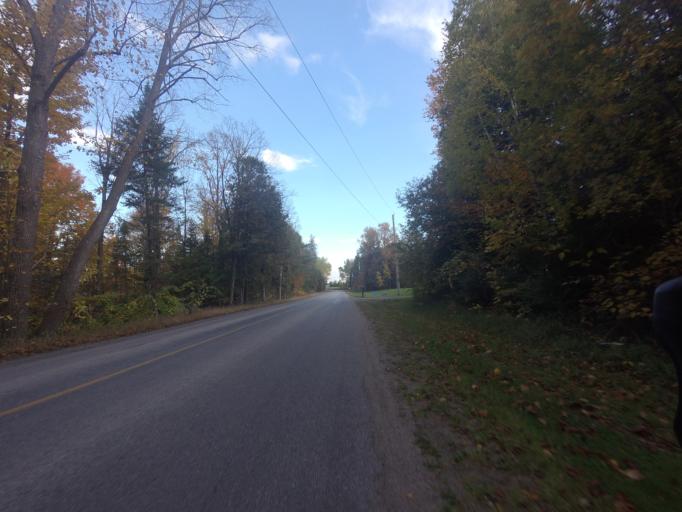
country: CA
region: Ontario
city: Pembroke
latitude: 45.5275
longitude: -77.0856
